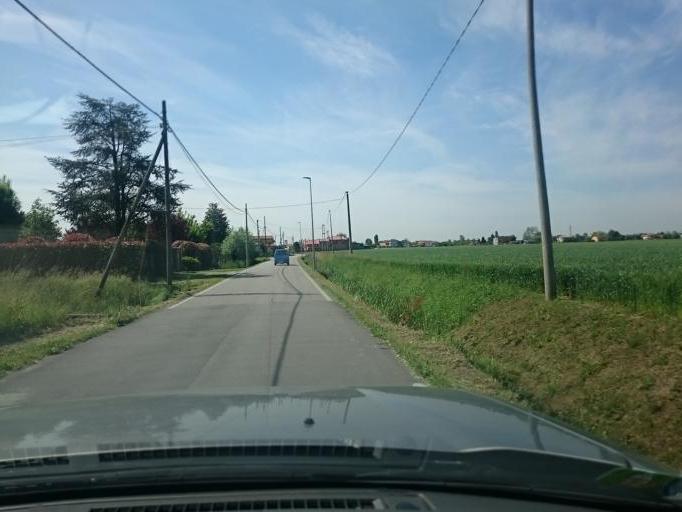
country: IT
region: Veneto
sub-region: Provincia di Padova
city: Bertipaglia
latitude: 45.3091
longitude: 11.8782
